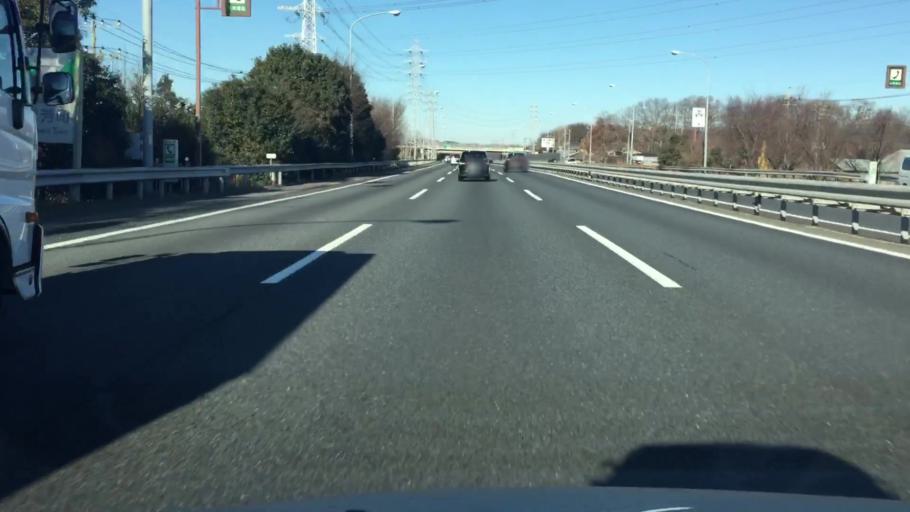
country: JP
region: Saitama
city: Oi
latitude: 35.8218
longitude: 139.5192
